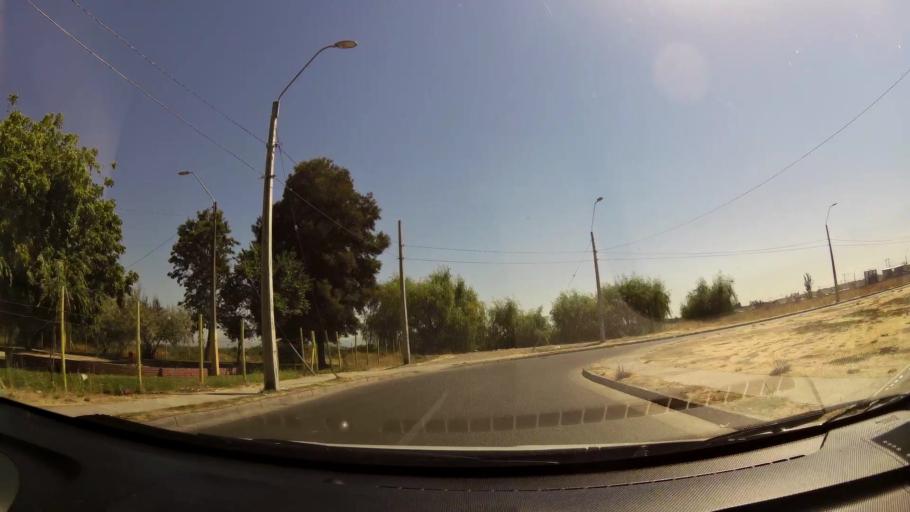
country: CL
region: Maule
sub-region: Provincia de Curico
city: Curico
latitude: -34.9641
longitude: -71.2401
